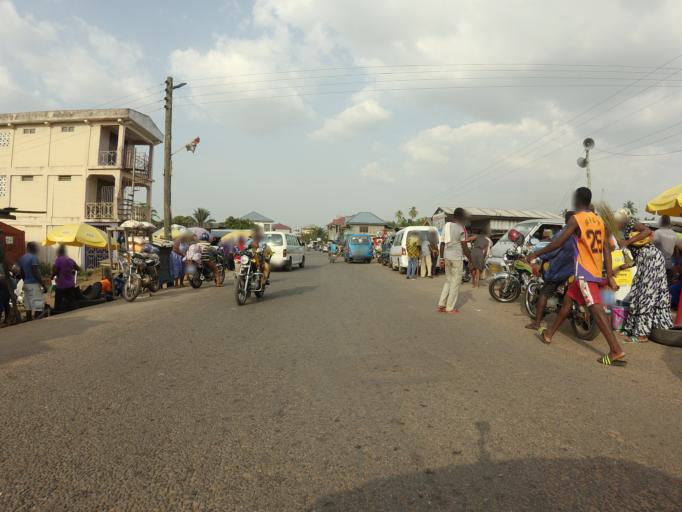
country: GH
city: Akropong
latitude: 6.2539
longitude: 0.1336
